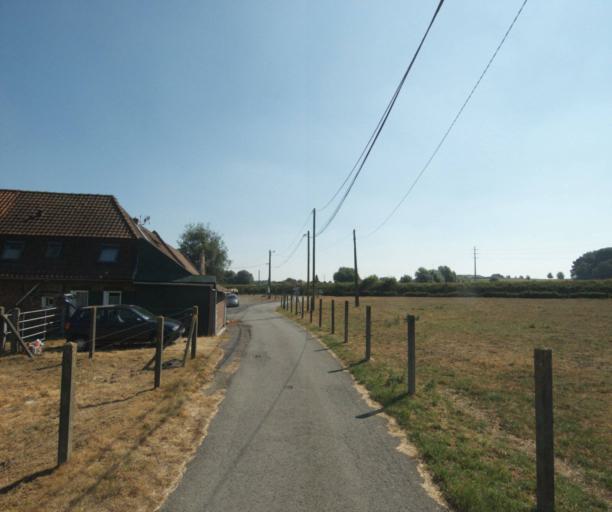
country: FR
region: Nord-Pas-de-Calais
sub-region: Departement du Nord
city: Bousbecque
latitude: 50.7689
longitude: 3.0902
